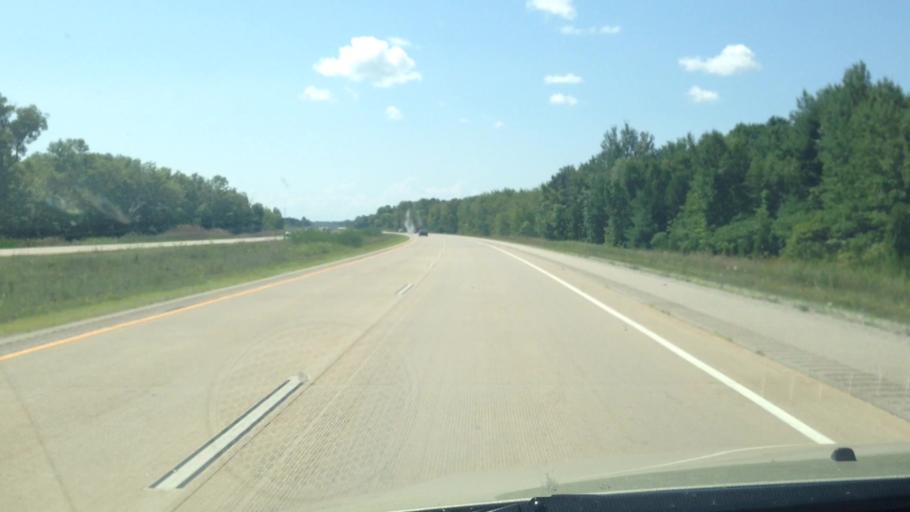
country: US
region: Wisconsin
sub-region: Oconto County
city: Oconto
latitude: 44.9667
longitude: -87.8720
